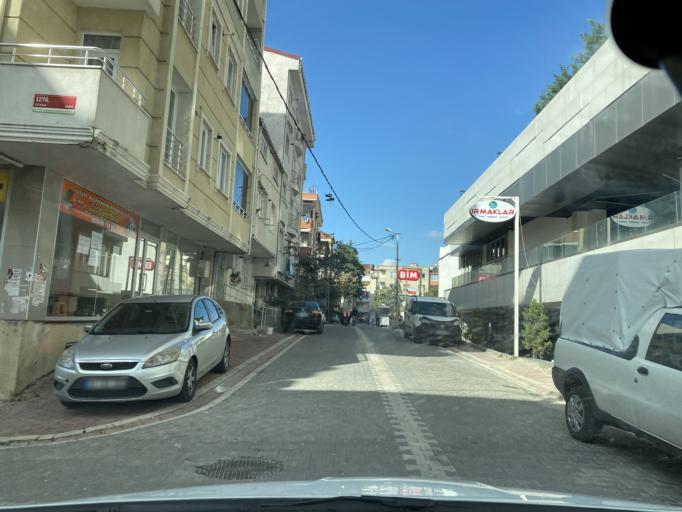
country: TR
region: Istanbul
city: Esenyurt
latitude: 41.0304
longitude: 28.6681
